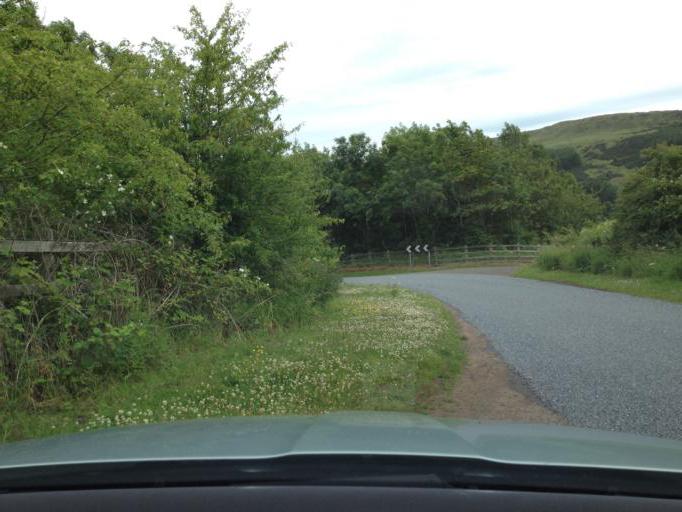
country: GB
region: Scotland
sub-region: Perth and Kinross
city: Bridge of Earn
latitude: 56.3270
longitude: -3.3996
